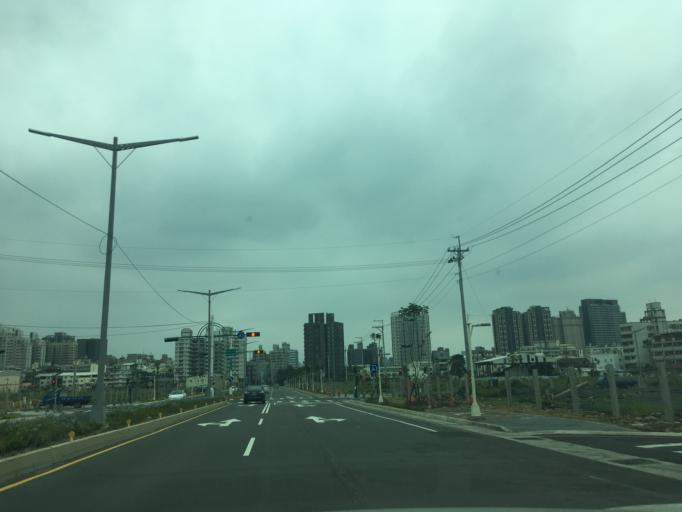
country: TW
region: Taiwan
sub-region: Taichung City
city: Taichung
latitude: 24.1814
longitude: 120.6769
